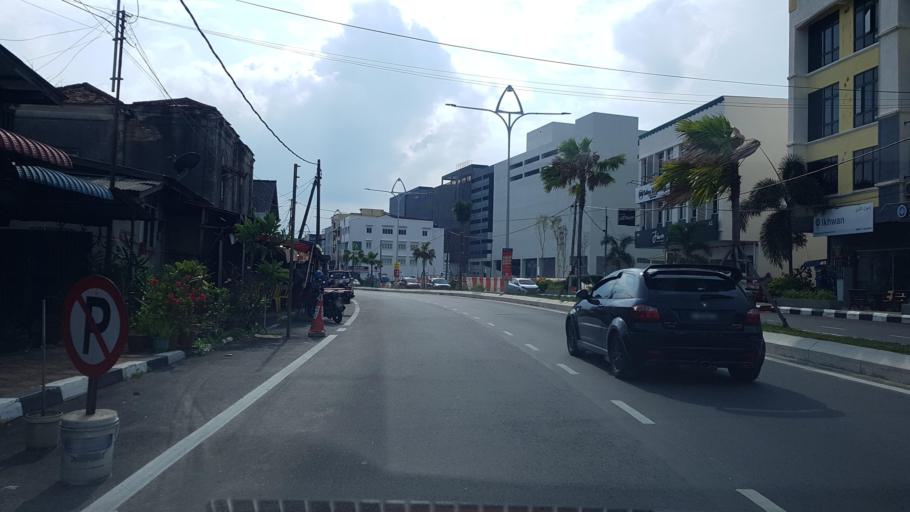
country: MY
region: Terengganu
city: Kuala Terengganu
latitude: 5.3357
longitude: 103.1453
